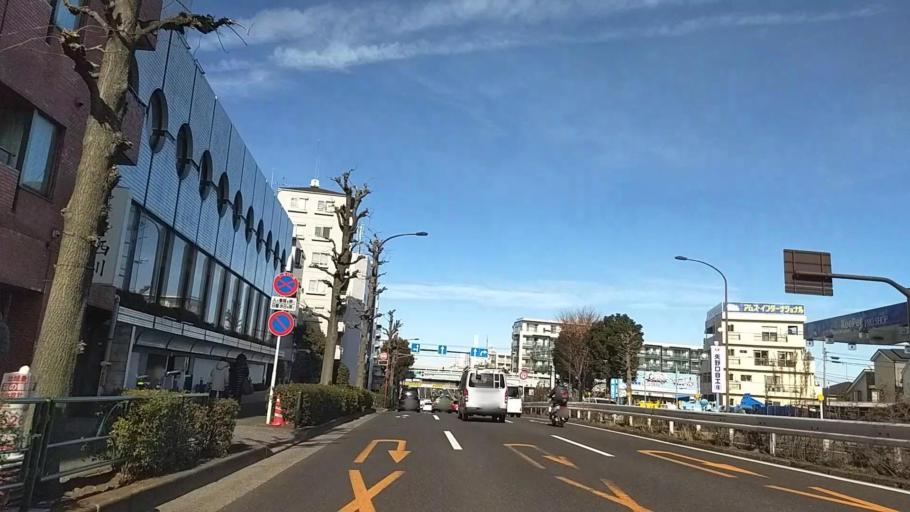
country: JP
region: Tokyo
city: Mitaka-shi
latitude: 35.6442
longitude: 139.6183
